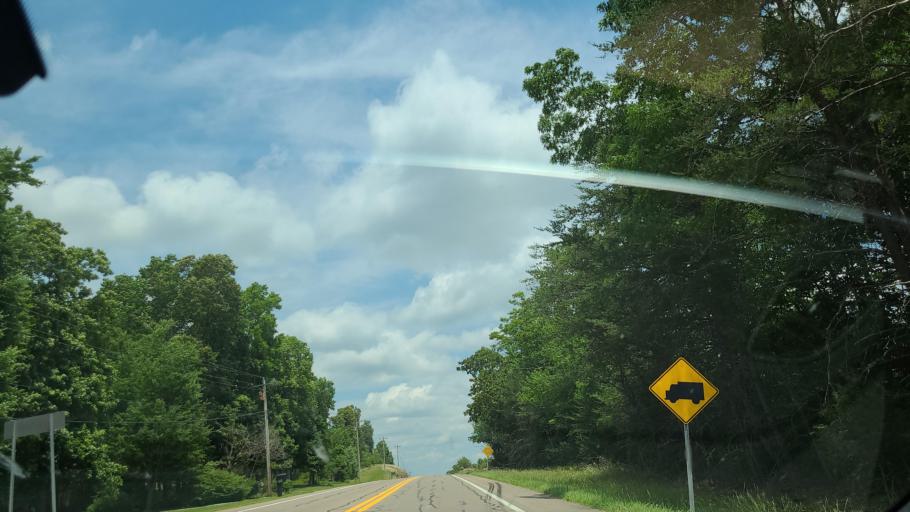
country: US
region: Tennessee
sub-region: Cumberland County
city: Lake Tansi
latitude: 35.8417
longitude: -85.0174
